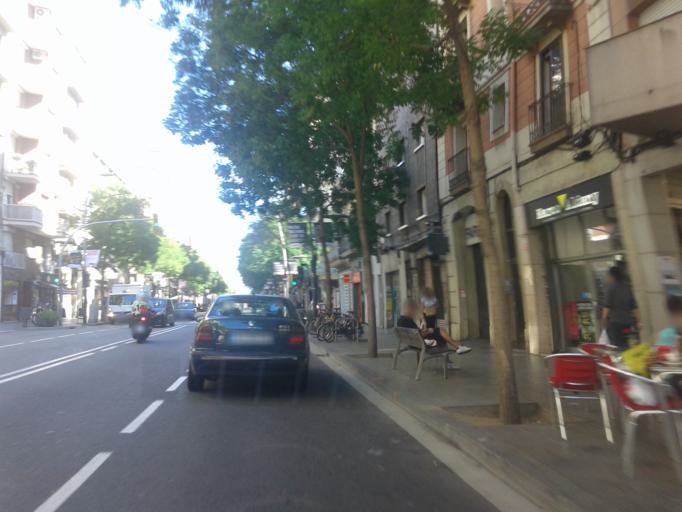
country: ES
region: Catalonia
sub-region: Provincia de Barcelona
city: Sants-Montjuic
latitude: 41.3752
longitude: 2.1454
